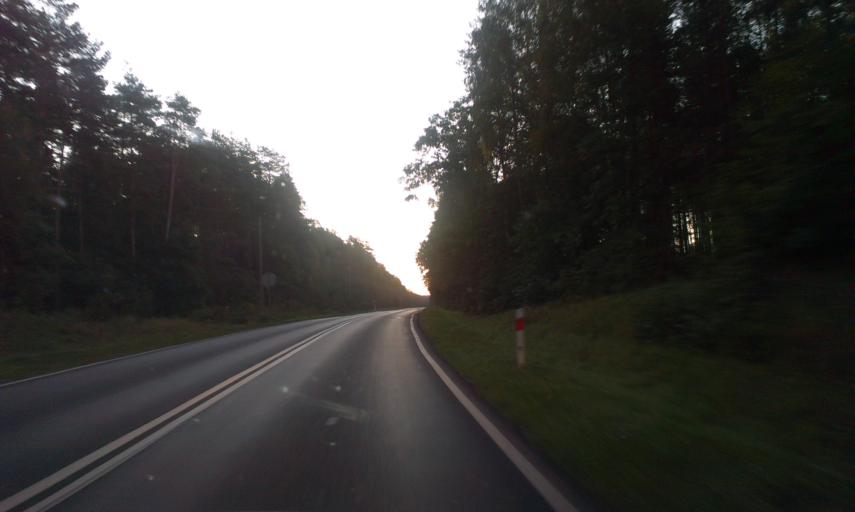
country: PL
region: Kujawsko-Pomorskie
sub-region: Powiat tucholski
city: Tuchola
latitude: 53.5544
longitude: 17.9077
